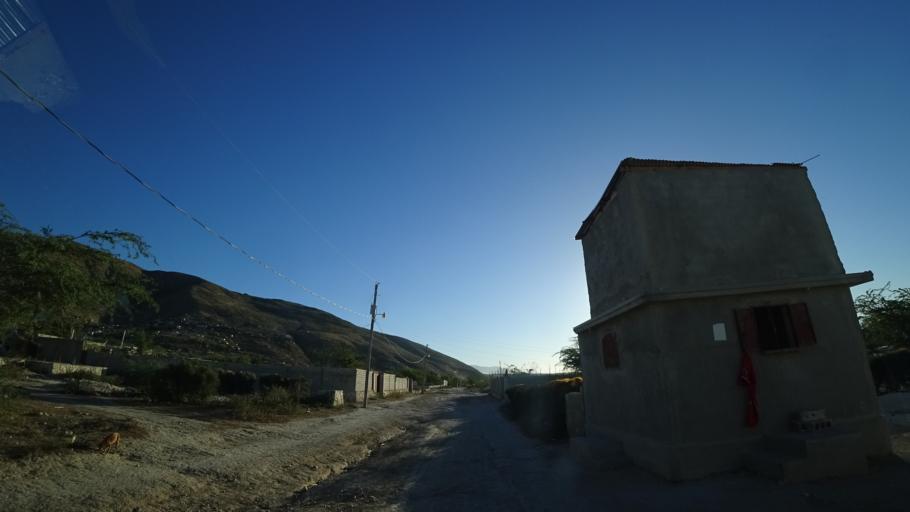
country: HT
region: Ouest
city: Croix des Bouquets
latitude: 18.6627
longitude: -72.2262
